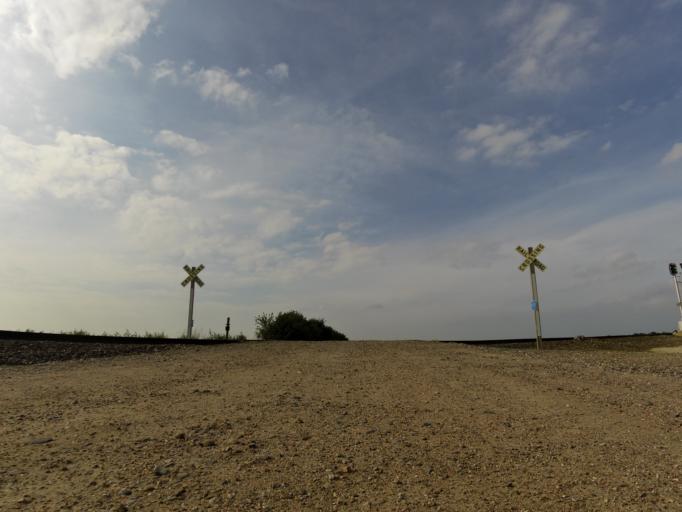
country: US
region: Kansas
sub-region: Reno County
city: South Hutchinson
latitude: 37.9781
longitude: -98.0687
